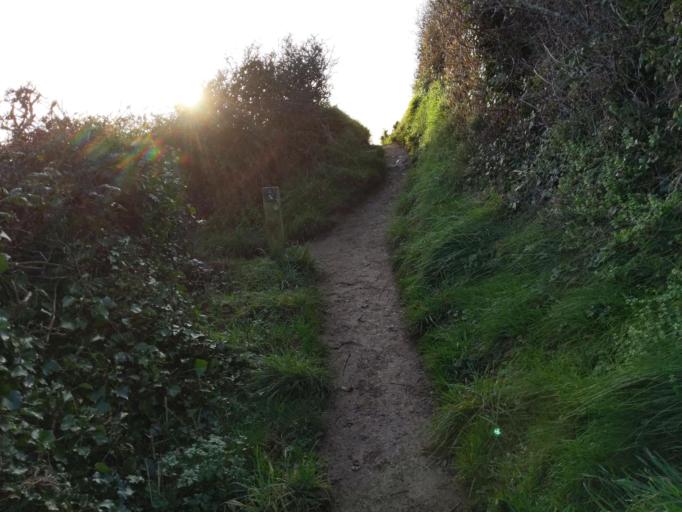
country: GB
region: England
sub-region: Cornwall
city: Fowey
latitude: 50.3252
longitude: -4.6240
